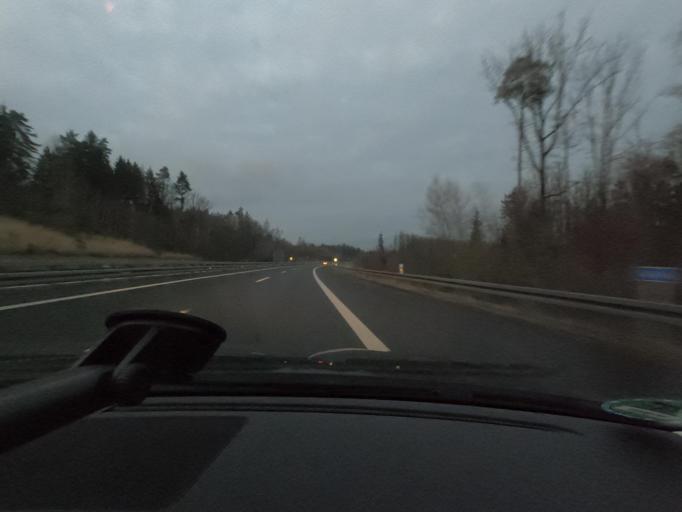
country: DE
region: Bavaria
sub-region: Upper Franconia
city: Untersiemau
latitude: 50.1706
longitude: 11.0077
